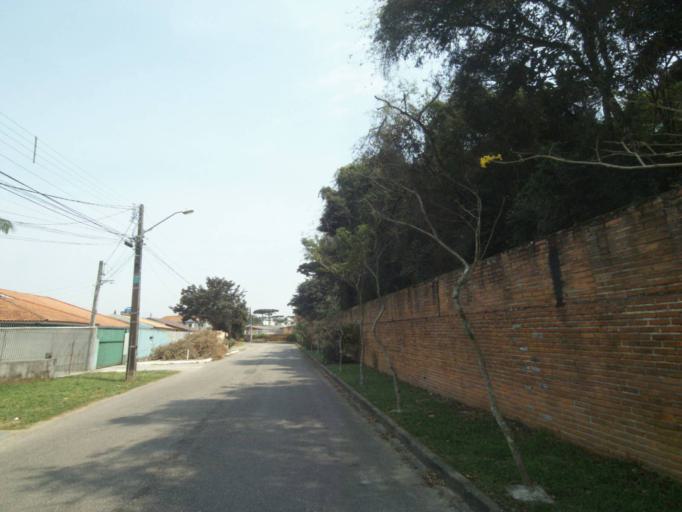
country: BR
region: Parana
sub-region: Sao Jose Dos Pinhais
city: Sao Jose dos Pinhais
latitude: -25.4910
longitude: -49.2105
